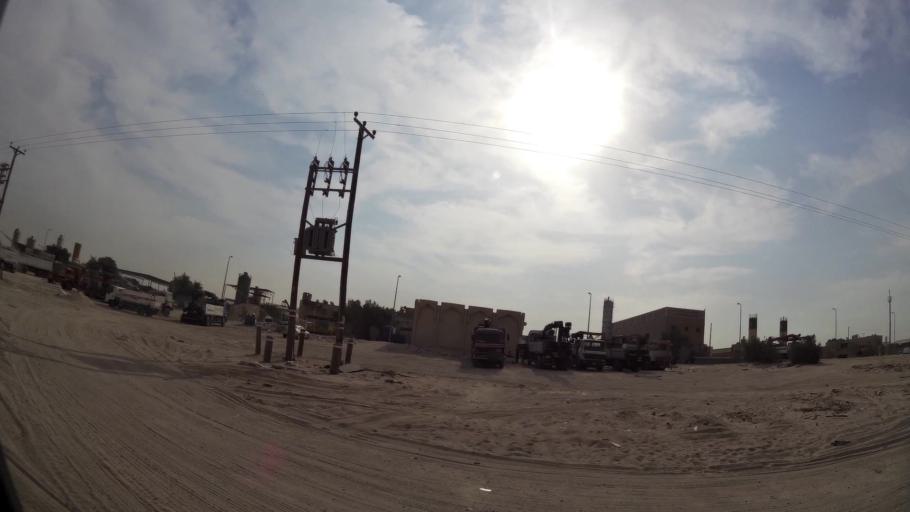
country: KW
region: Muhafazat al Jahra'
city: Al Jahra'
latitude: 29.3072
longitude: 47.7414
